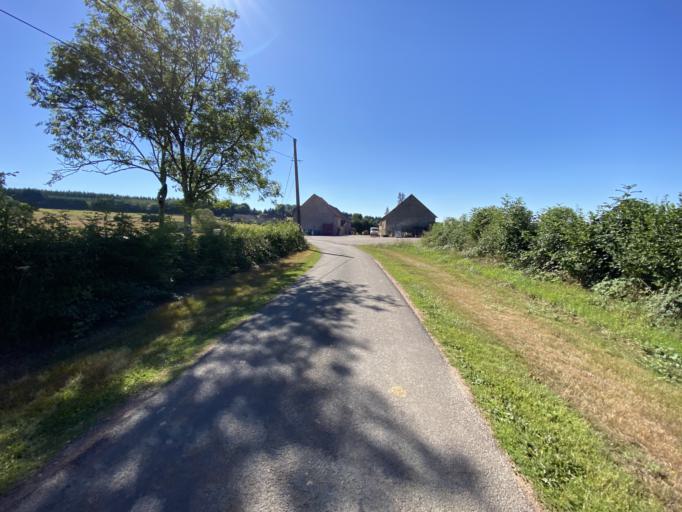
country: FR
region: Bourgogne
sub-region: Departement de la Cote-d'Or
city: Saulieu
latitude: 47.2728
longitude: 4.1803
